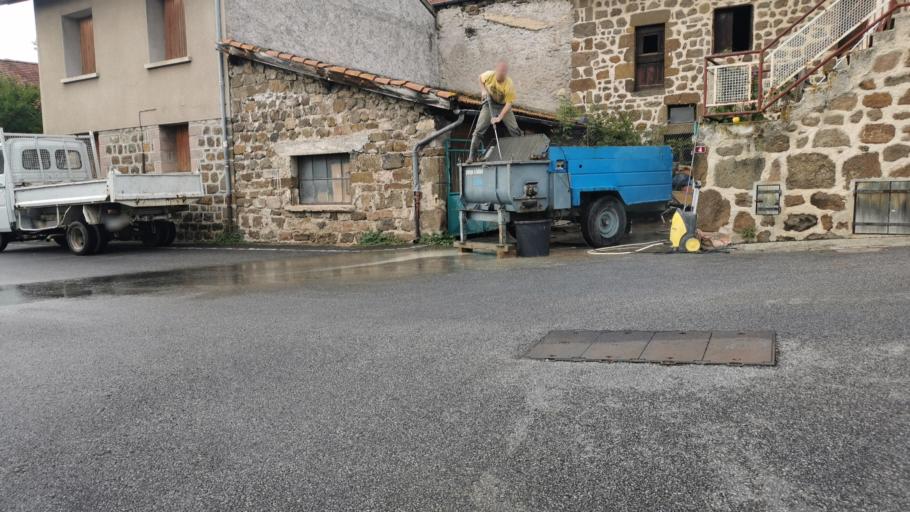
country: FR
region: Auvergne
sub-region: Departement de la Haute-Loire
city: Polignac
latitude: 45.0696
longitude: 3.8626
